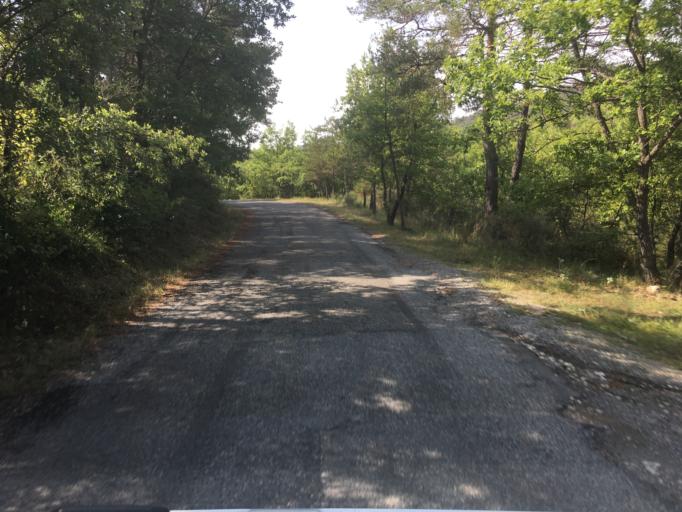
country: FR
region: Provence-Alpes-Cote d'Azur
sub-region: Departement des Alpes-de-Haute-Provence
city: Mallemoisson
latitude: 43.9233
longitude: 6.1912
